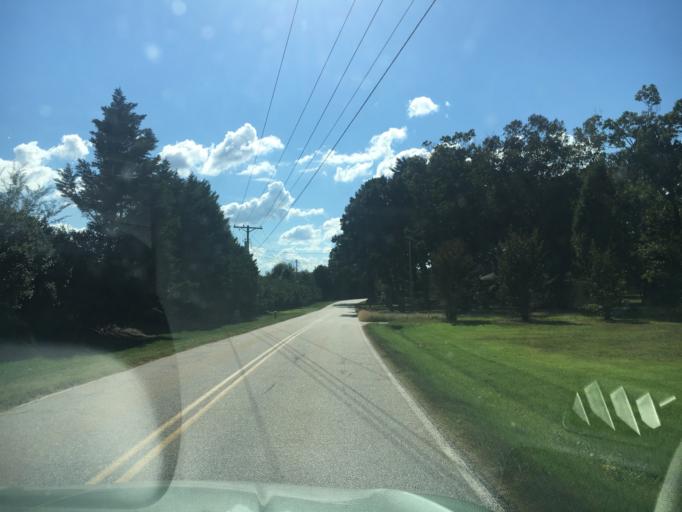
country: US
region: South Carolina
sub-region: Greenville County
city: Five Forks
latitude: 34.8190
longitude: -82.2109
